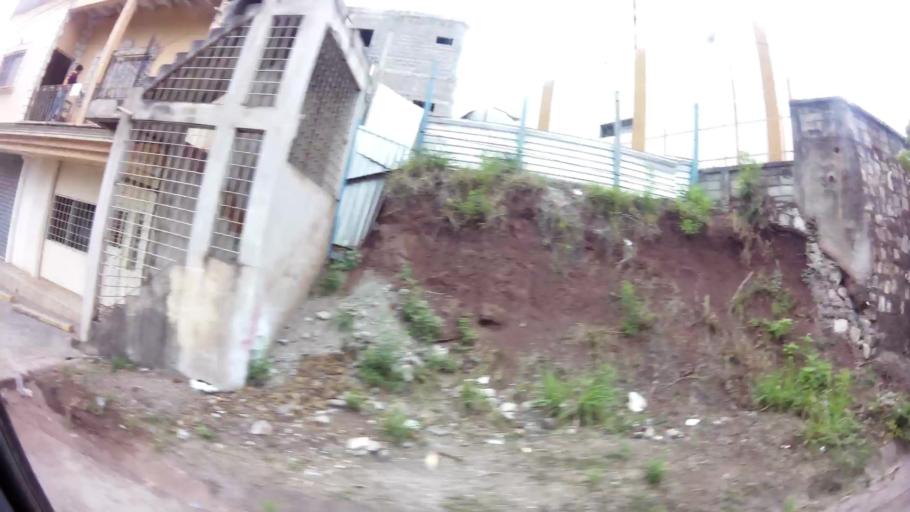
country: HN
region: Francisco Morazan
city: Tegucigalpa
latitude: 14.0738
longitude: -87.1737
